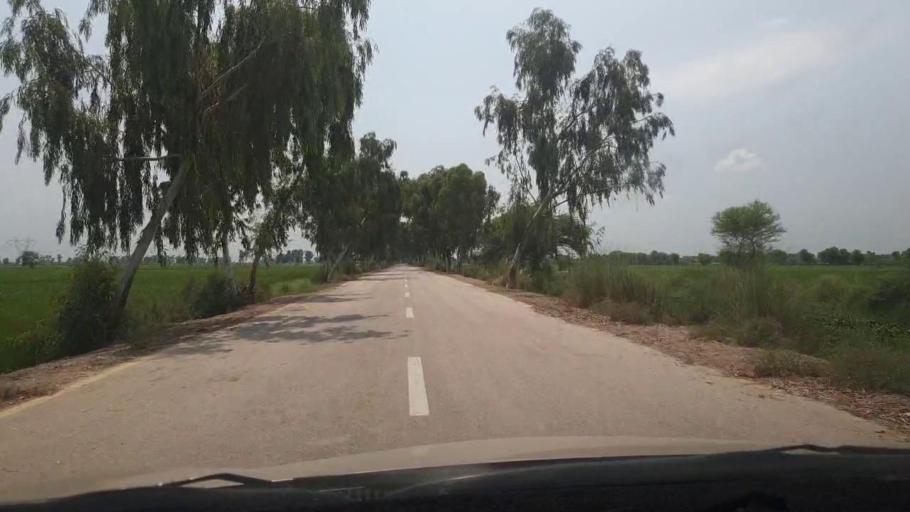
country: PK
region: Sindh
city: Naudero
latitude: 27.7058
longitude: 68.3385
